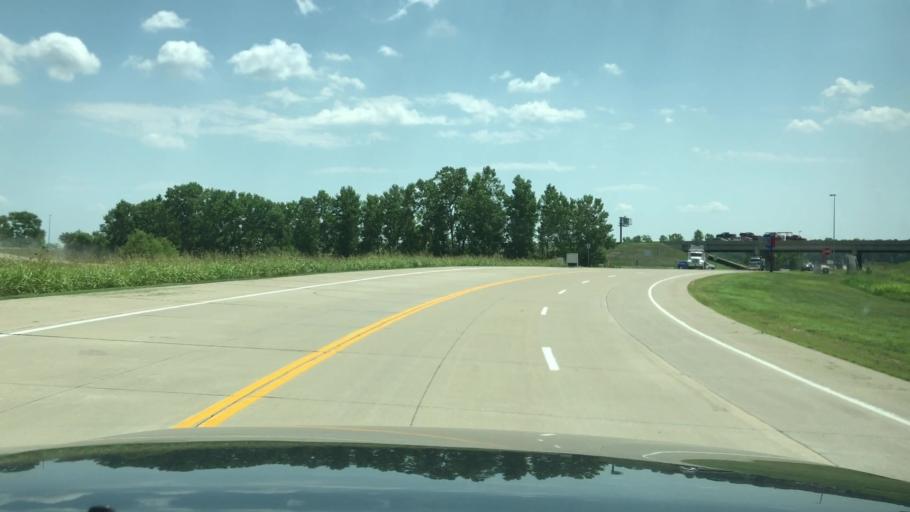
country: US
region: Missouri
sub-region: Saint Charles County
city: Saint Peters
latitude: 38.8198
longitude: -90.5621
